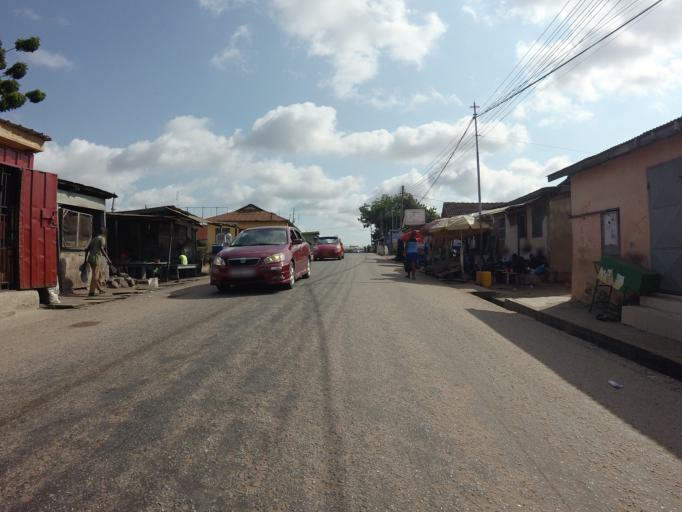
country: GH
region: Greater Accra
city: Dome
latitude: 5.6119
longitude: -0.2334
